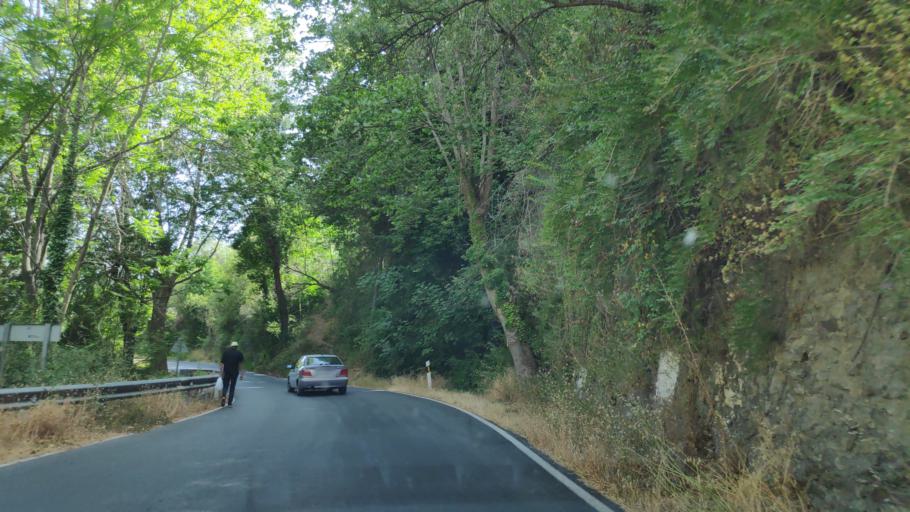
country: ES
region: Andalusia
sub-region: Provincia de Granada
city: Pampaneira
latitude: 36.9422
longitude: -3.3644
